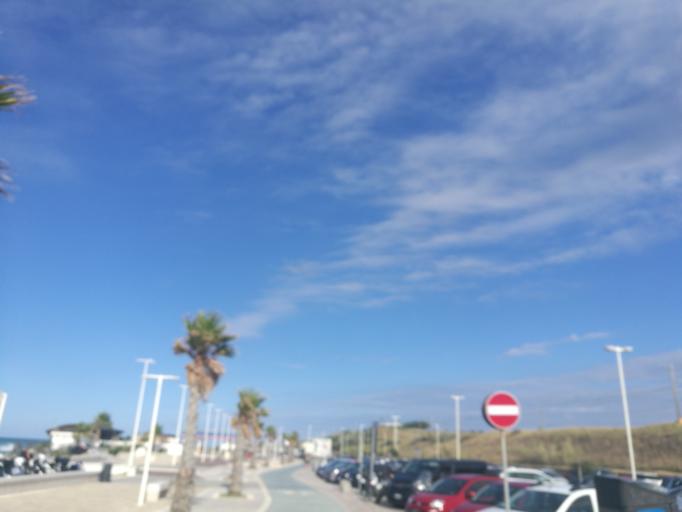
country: IT
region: Molise
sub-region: Provincia di Campobasso
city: Termoli
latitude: 42.0076
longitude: 14.9685
